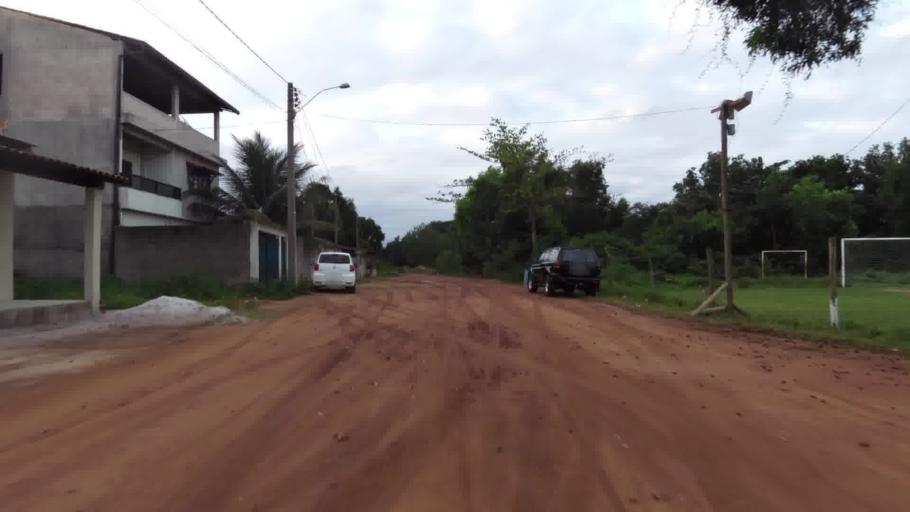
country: BR
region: Espirito Santo
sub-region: Piuma
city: Piuma
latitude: -20.8092
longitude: -40.6313
